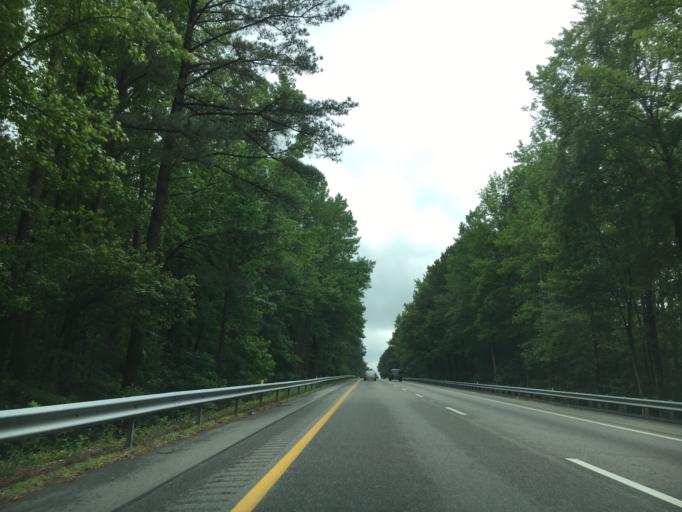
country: US
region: Virginia
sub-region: Brunswick County
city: Lawrenceville
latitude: 36.8566
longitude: -77.8534
